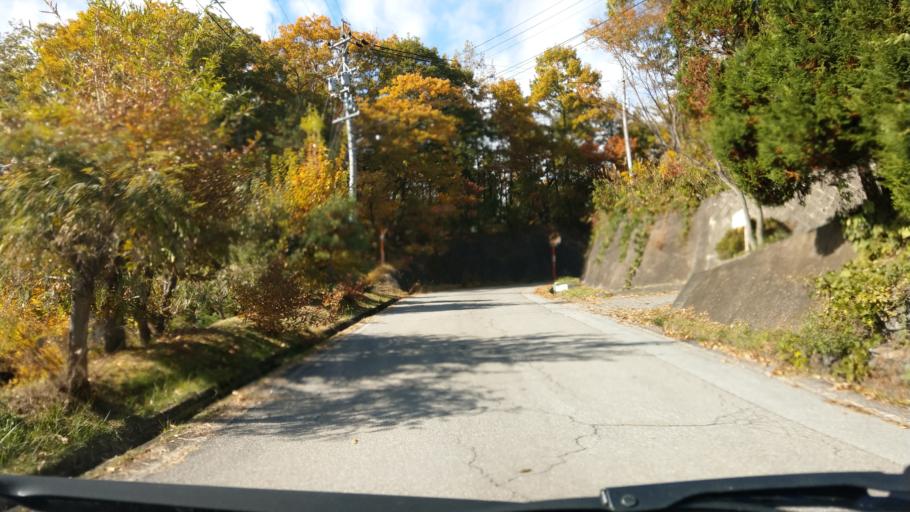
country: JP
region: Nagano
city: Komoro
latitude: 36.3074
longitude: 138.4325
